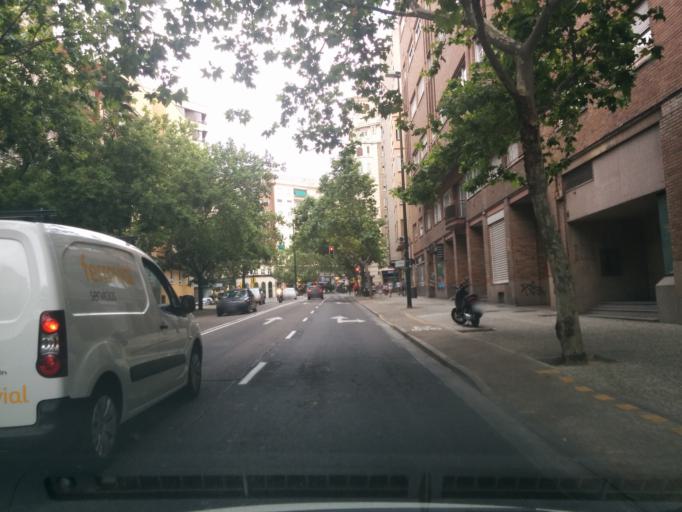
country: ES
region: Aragon
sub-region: Provincia de Zaragoza
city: Zaragoza
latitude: 41.6403
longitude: -0.8880
